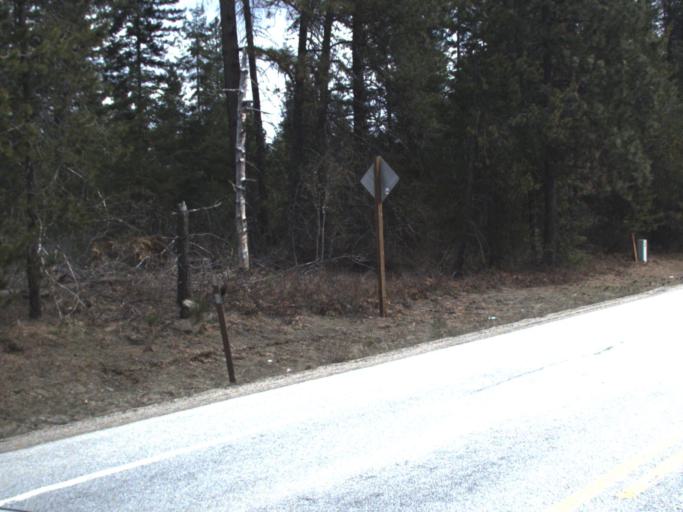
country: US
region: Washington
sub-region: Pend Oreille County
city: Newport
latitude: 48.2187
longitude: -117.0927
